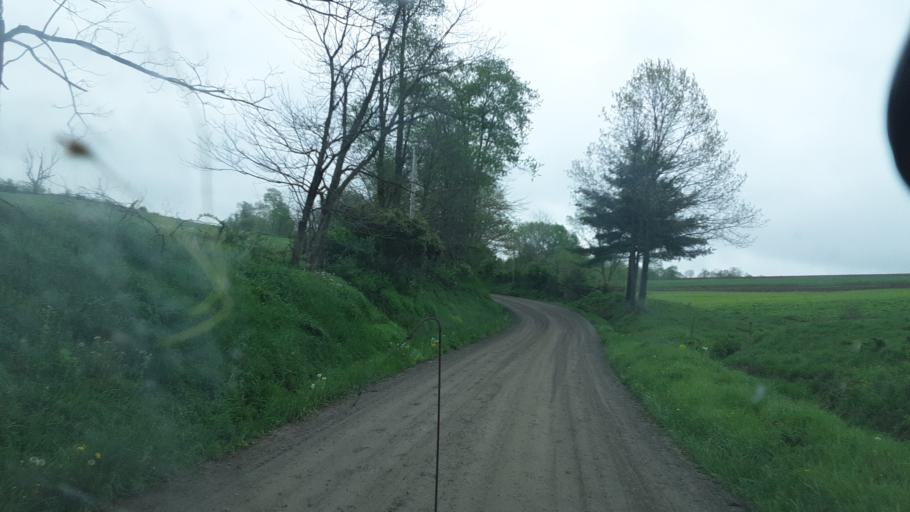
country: US
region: Ohio
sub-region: Tuscarawas County
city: Sugarcreek
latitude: 40.4686
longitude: -81.7902
